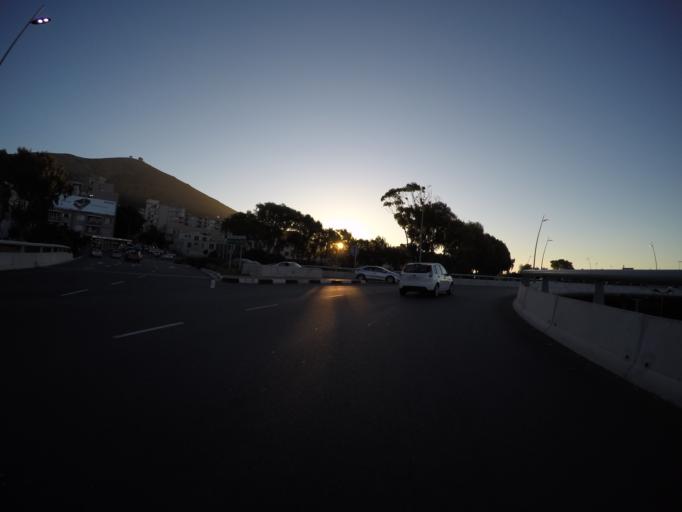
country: ZA
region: Western Cape
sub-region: City of Cape Town
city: Cape Town
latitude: -33.9074
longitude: 18.4110
